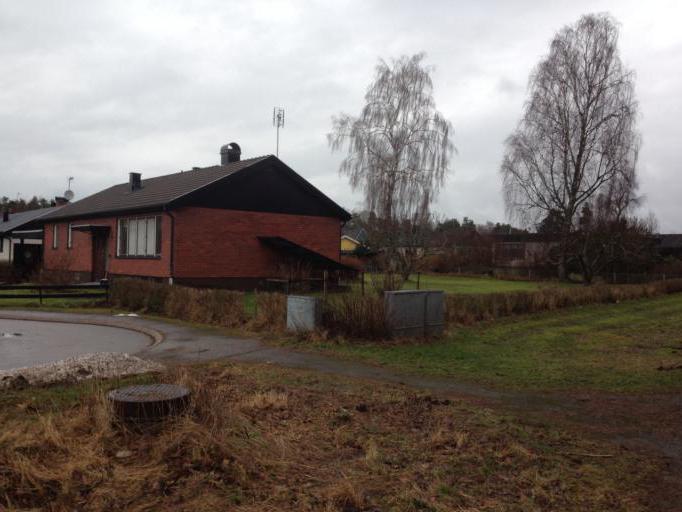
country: SE
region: Vaestra Goetaland
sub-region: Mariestads Kommun
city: Mariestad
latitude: 58.6921
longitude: 13.8051
